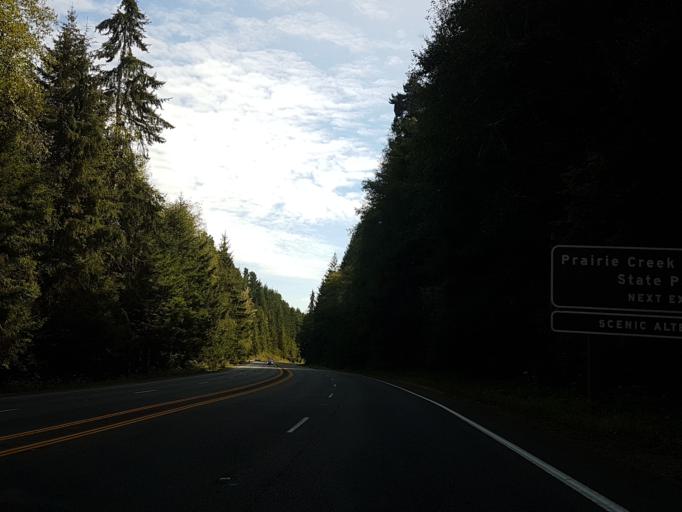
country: US
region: California
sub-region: Del Norte County
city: Bertsch-Oceanview
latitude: 41.4772
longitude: -124.0470
